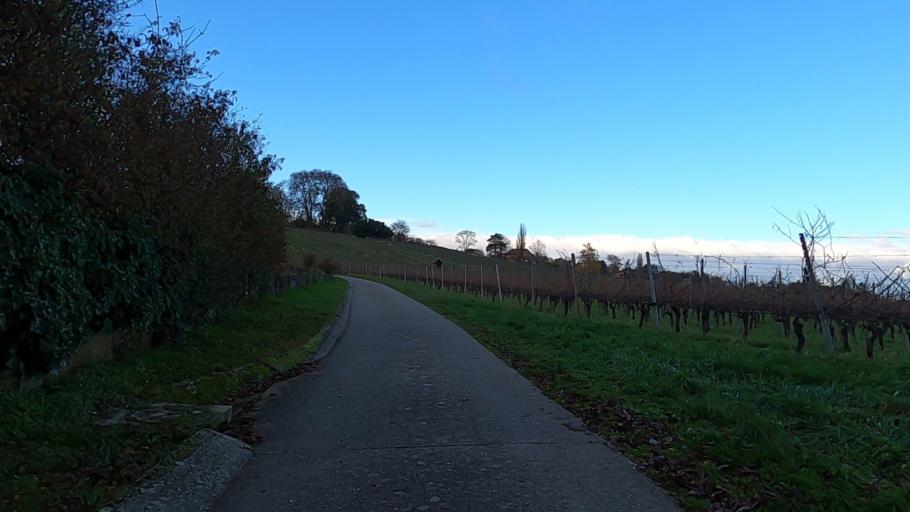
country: CH
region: Vaud
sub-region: Morges District
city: Saint-Prex
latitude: 46.5148
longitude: 6.4618
